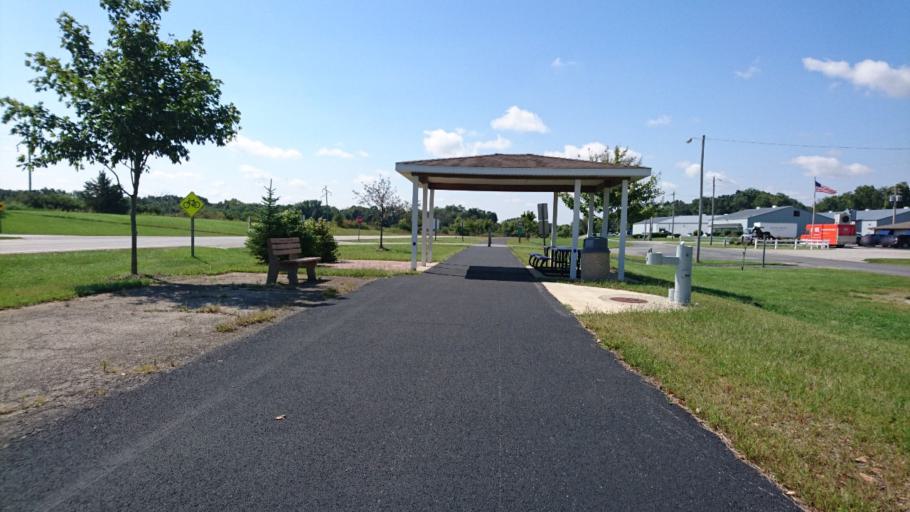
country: US
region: Illinois
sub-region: McLean County
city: Lexington
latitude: 40.6361
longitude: -88.7948
